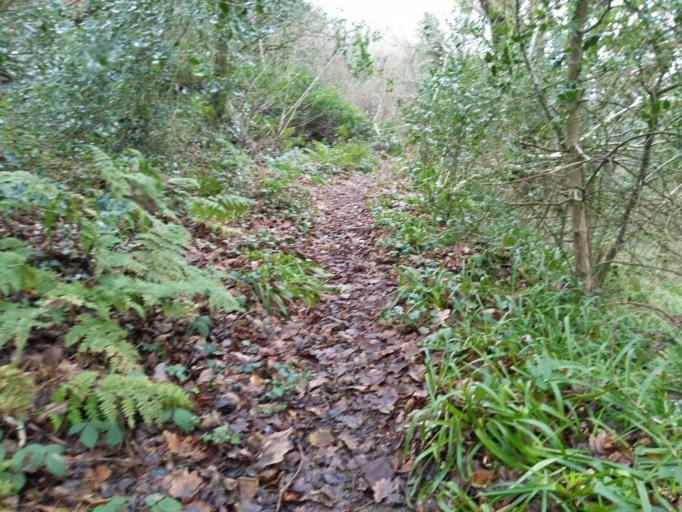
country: GB
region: England
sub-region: Cornwall
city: Fowey
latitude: 50.3324
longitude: -4.6278
